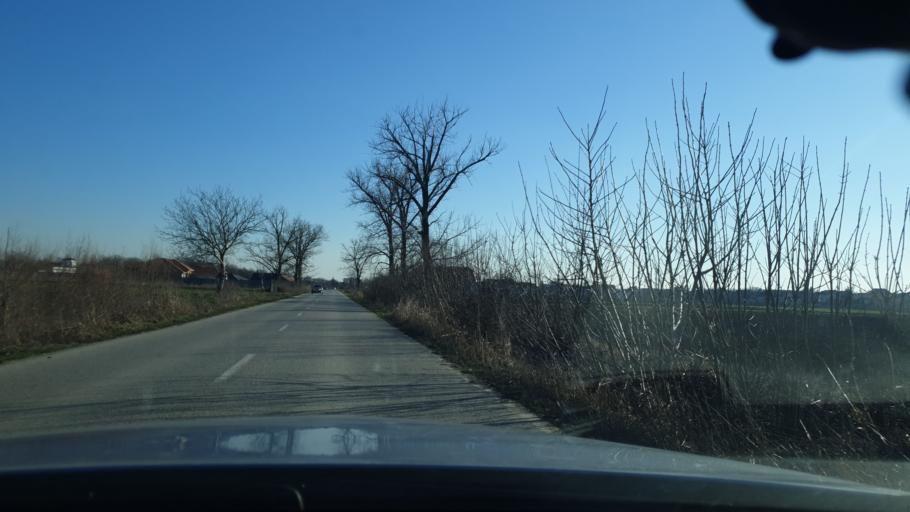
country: RS
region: Autonomna Pokrajina Vojvodina
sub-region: Sremski Okrug
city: Ruma
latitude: 45.0233
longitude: 19.8139
